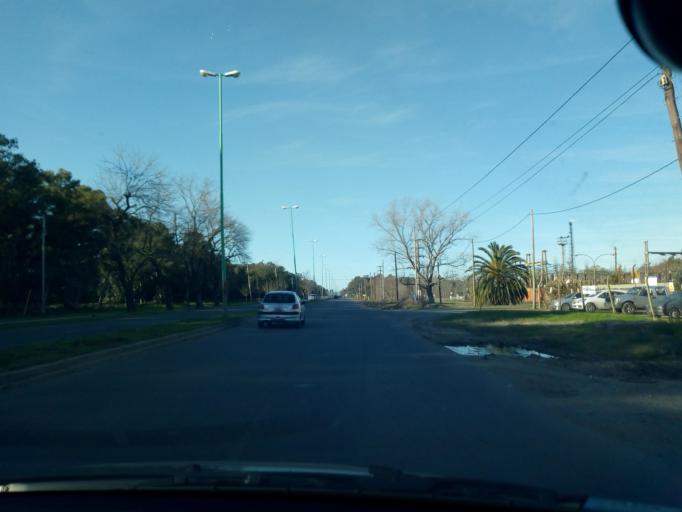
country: AR
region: Buenos Aires
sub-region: Partido de Ensenada
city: Ensenada
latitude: -34.8899
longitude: -57.9342
